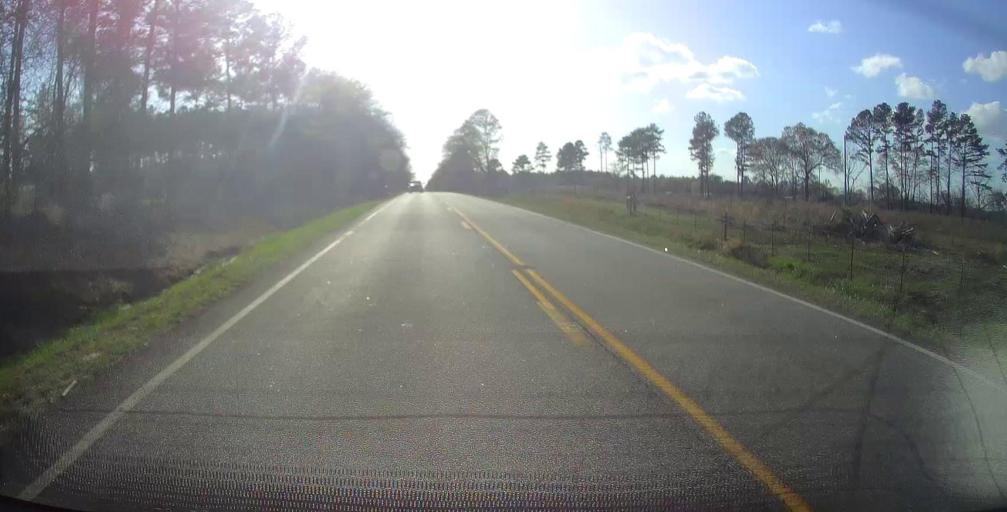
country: US
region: Georgia
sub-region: Montgomery County
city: Mount Vernon
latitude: 32.1859
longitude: -82.6502
